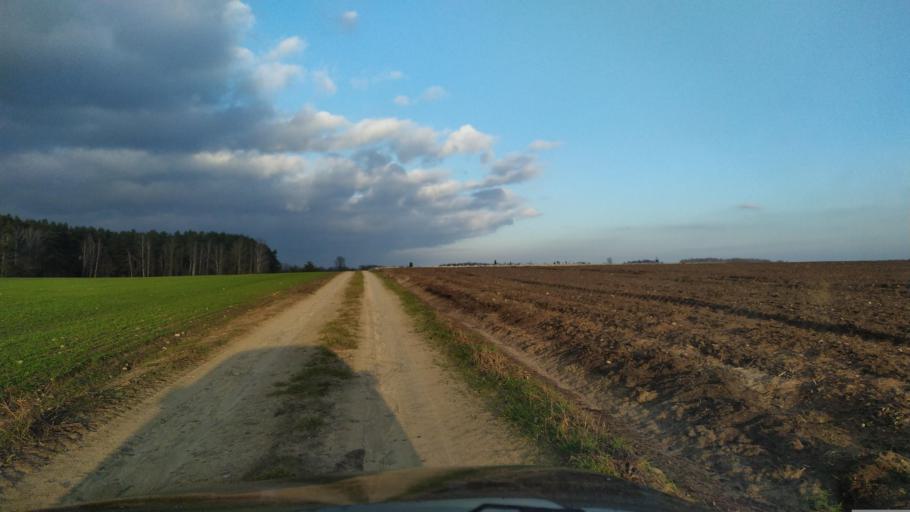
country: BY
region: Brest
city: Kamyanyets
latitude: 52.3807
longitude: 23.7804
